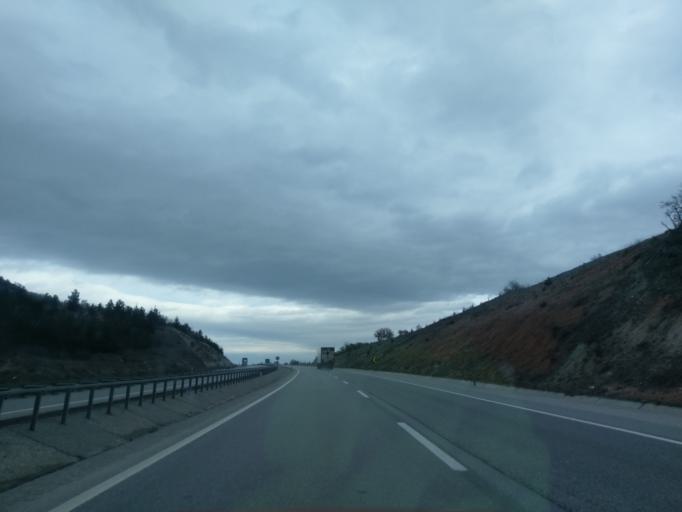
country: TR
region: Kuetahya
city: Sabuncu
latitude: 39.5933
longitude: 30.1419
